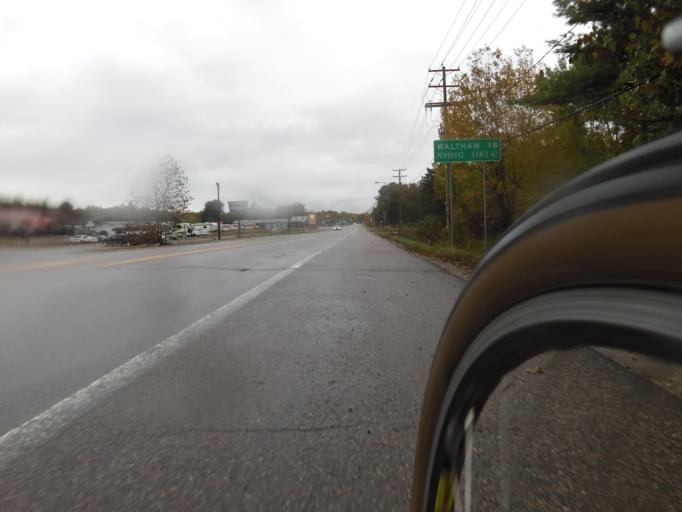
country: CA
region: Quebec
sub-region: Outaouais
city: Fort-Coulonge
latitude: 45.8515
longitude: -76.7308
